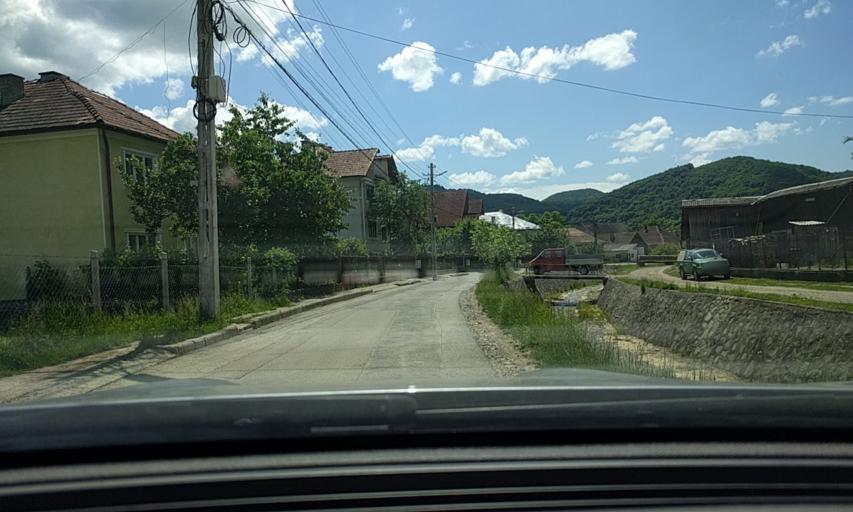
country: RO
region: Bistrita-Nasaud
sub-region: Oras Nasaud
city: Nasaud
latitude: 47.2879
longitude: 24.4051
